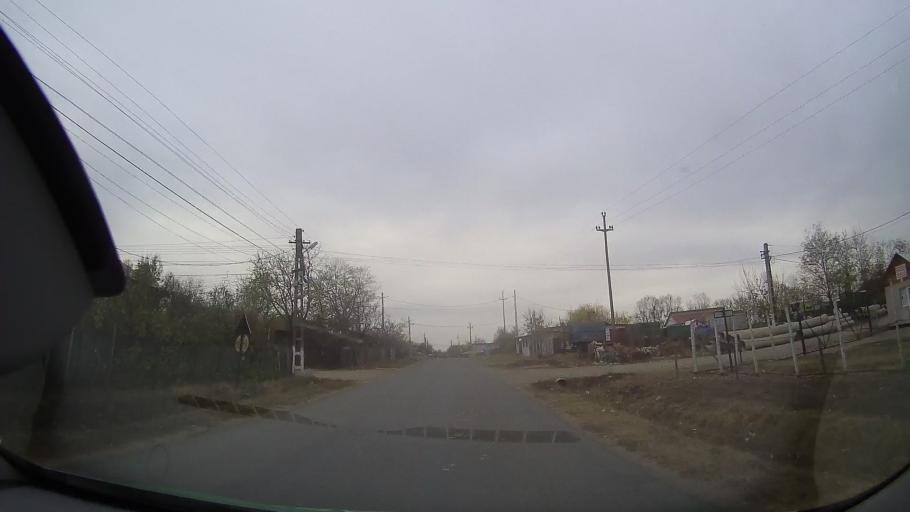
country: RO
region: Buzau
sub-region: Comuna Largu
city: Largu
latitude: 44.9745
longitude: 27.1494
